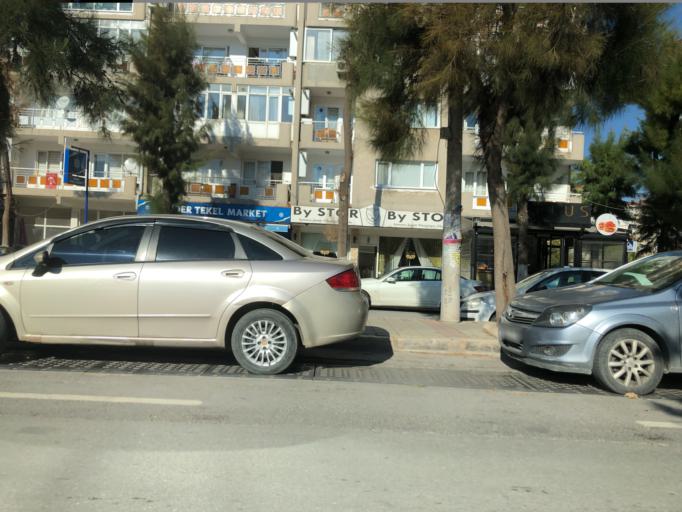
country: TR
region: Izmir
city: Bornova
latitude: 38.4580
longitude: 27.1869
